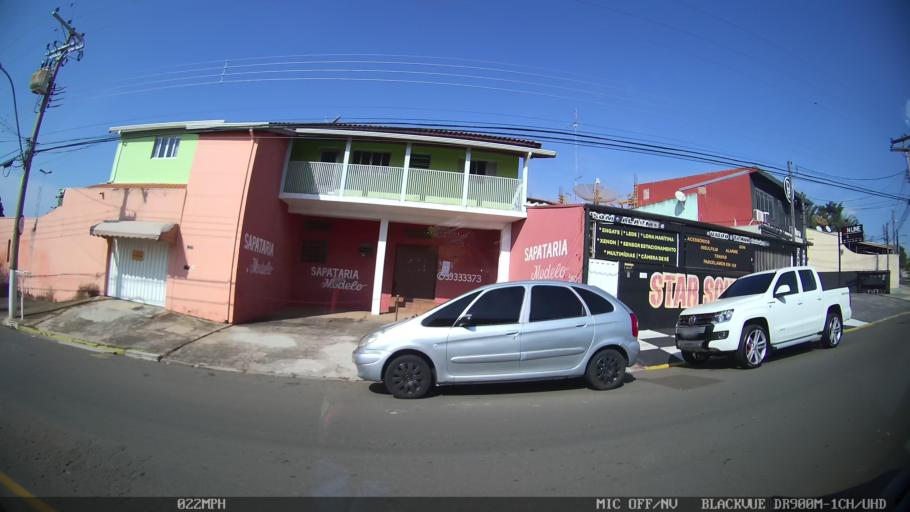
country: BR
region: Sao Paulo
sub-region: Paulinia
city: Paulinia
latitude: -22.7708
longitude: -47.1586
